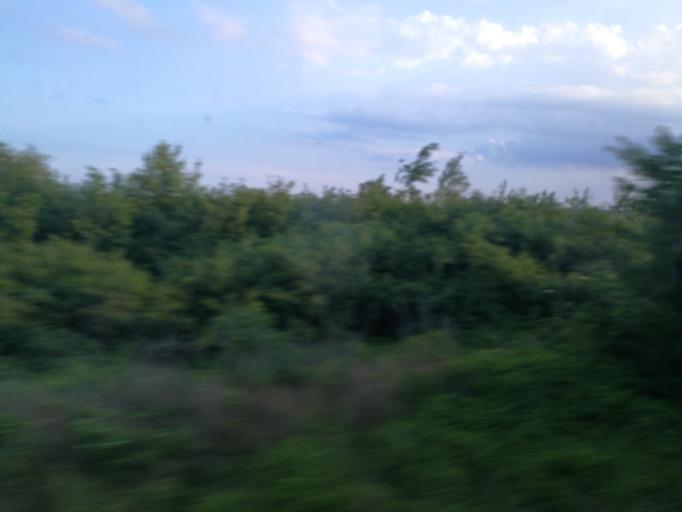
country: RO
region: Dambovita
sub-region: Comuna Contesti
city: Contesti
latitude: 44.6602
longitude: 25.6153
